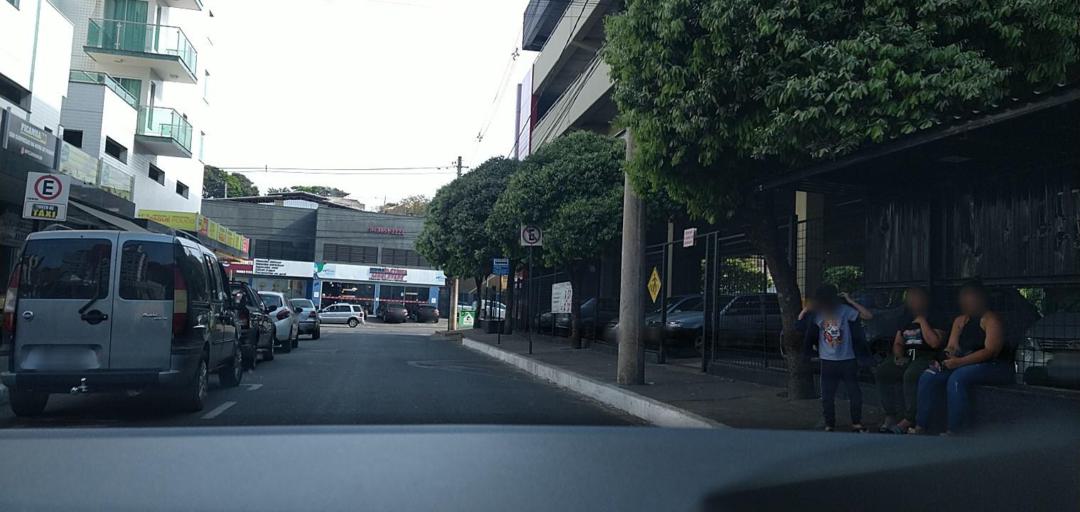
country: BR
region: Minas Gerais
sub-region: Joao Monlevade
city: Joao Monlevade
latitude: -19.8073
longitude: -43.1830
